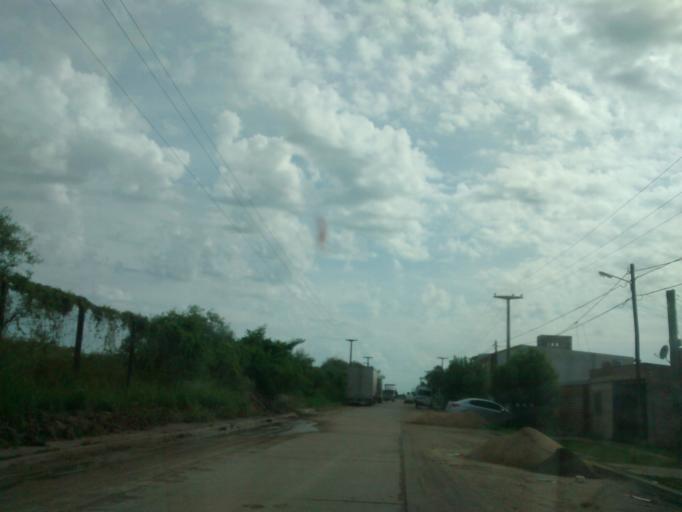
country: AR
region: Chaco
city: Resistencia
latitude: -27.4131
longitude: -58.9647
